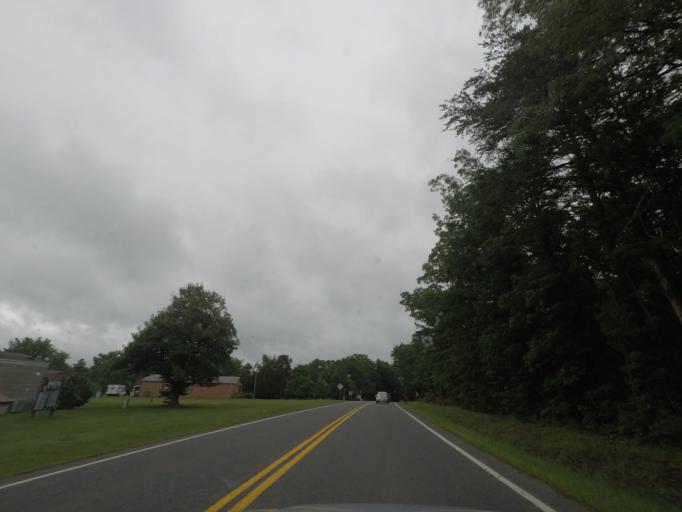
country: US
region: Virginia
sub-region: Fluvanna County
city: Palmyra
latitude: 37.9416
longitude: -78.2448
